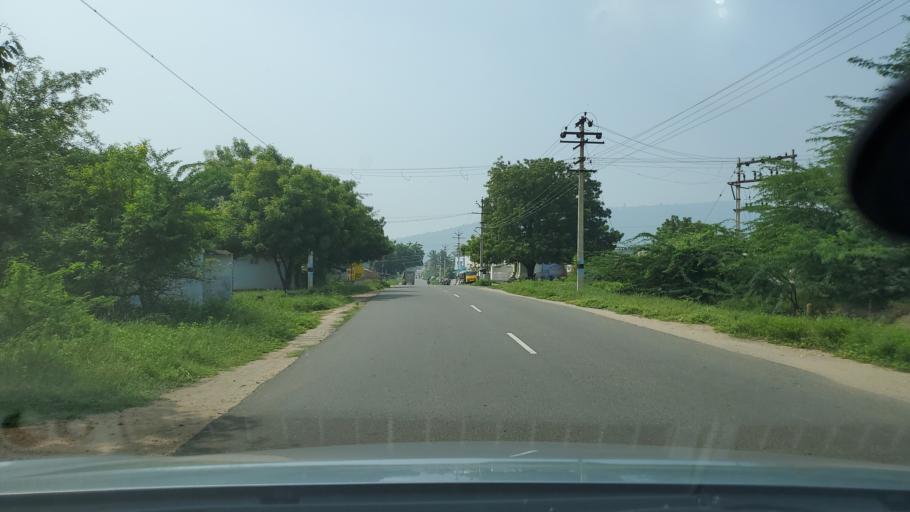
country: IN
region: Tamil Nadu
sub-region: Erode
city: Chennimalai
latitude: 11.1752
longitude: 77.6057
